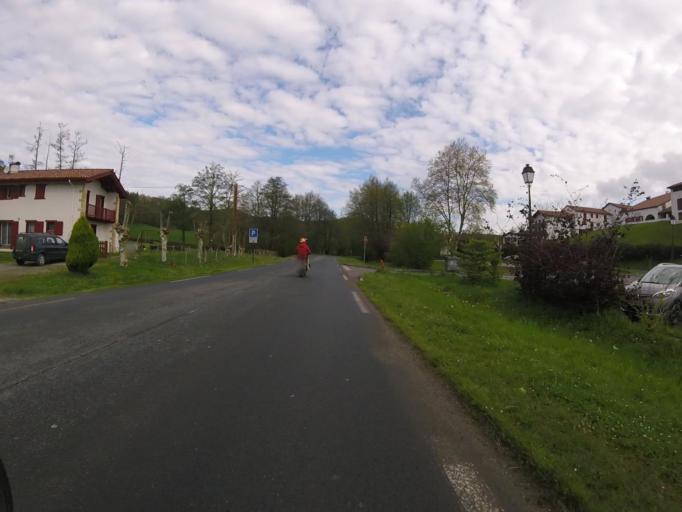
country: FR
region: Aquitaine
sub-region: Departement des Pyrenees-Atlantiques
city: Sare
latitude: 43.3122
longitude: -1.5842
